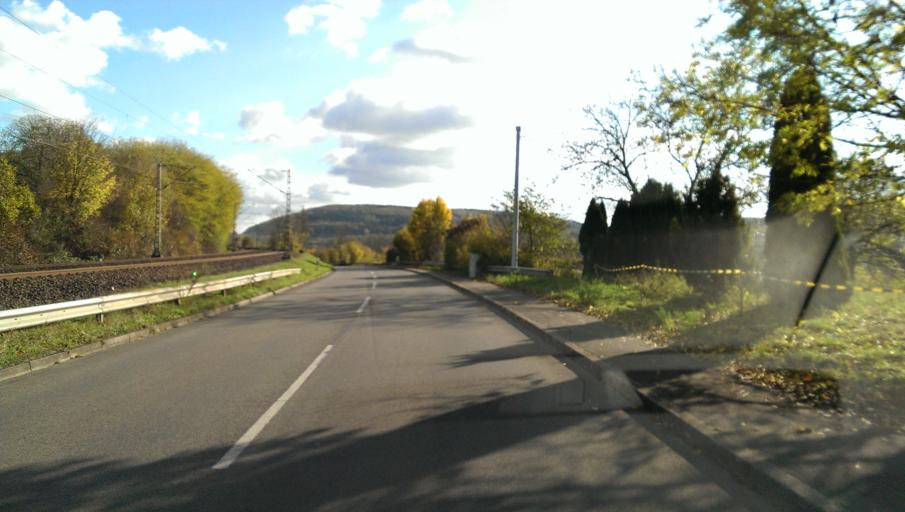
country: DE
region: Baden-Wuerttemberg
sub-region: Karlsruhe Region
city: Obrigheim
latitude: 49.3335
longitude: 9.1062
